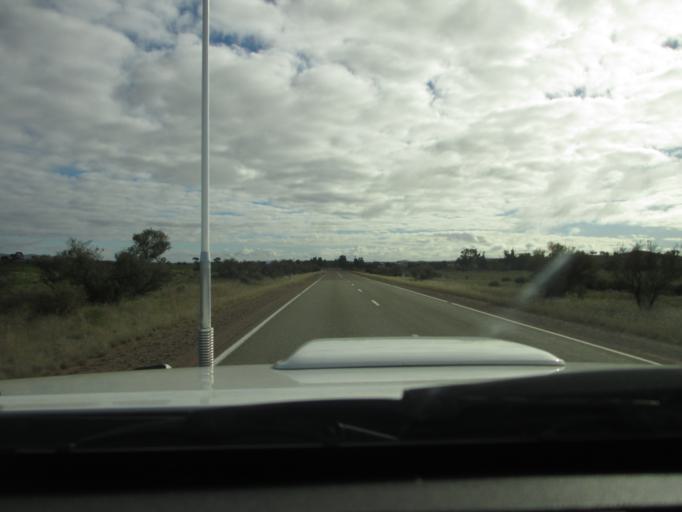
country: AU
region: South Australia
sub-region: Flinders Ranges
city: Quorn
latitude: -32.4912
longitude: 138.5465
